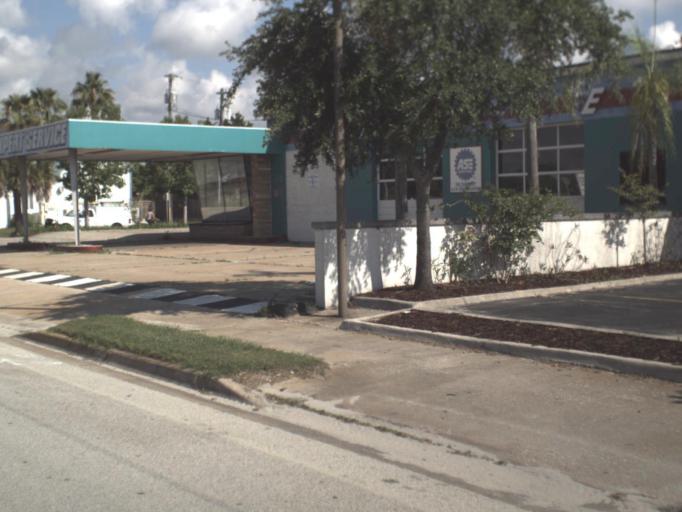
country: US
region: Florida
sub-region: Saint Johns County
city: Saint Augustine
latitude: 29.8915
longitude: -81.2988
